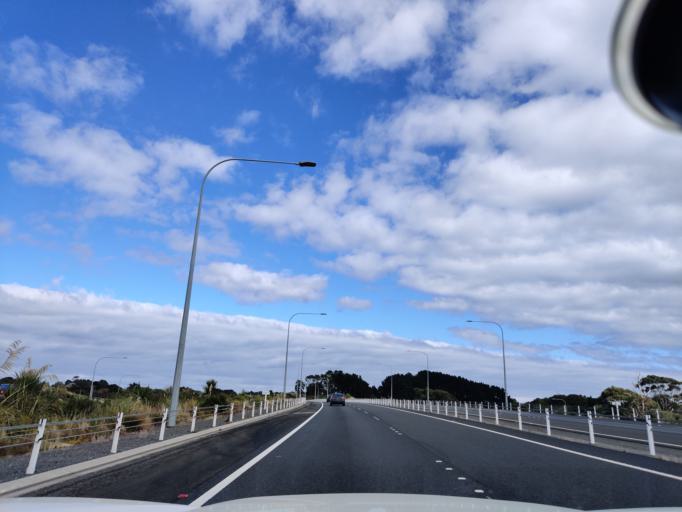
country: NZ
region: Wellington
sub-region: Kapiti Coast District
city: Paraparaumu
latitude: -40.8673
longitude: 175.0375
